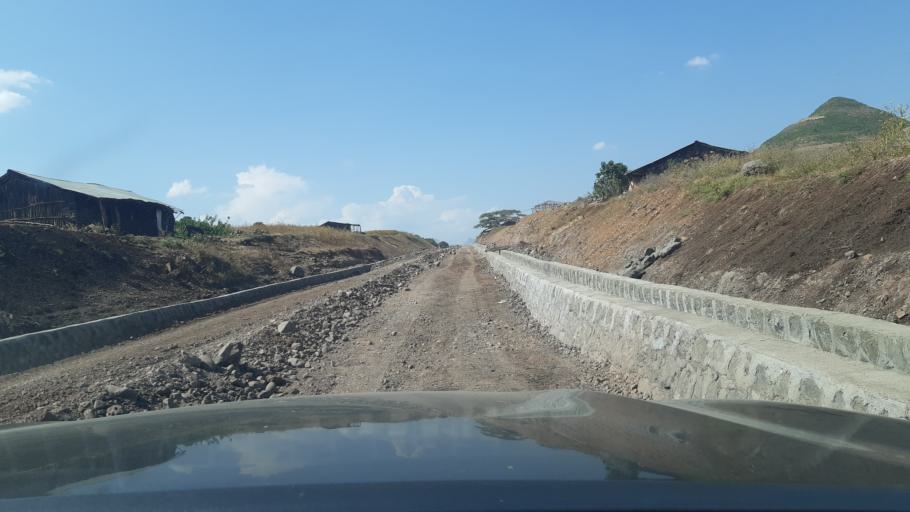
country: ET
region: Amhara
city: Dabat
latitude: 13.1605
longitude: 37.6075
